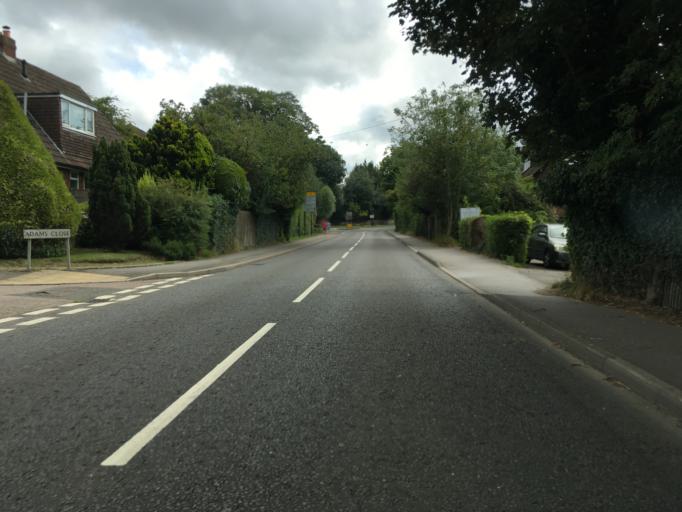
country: GB
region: England
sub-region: Kent
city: Tenterden
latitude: 51.0758
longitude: 0.6941
